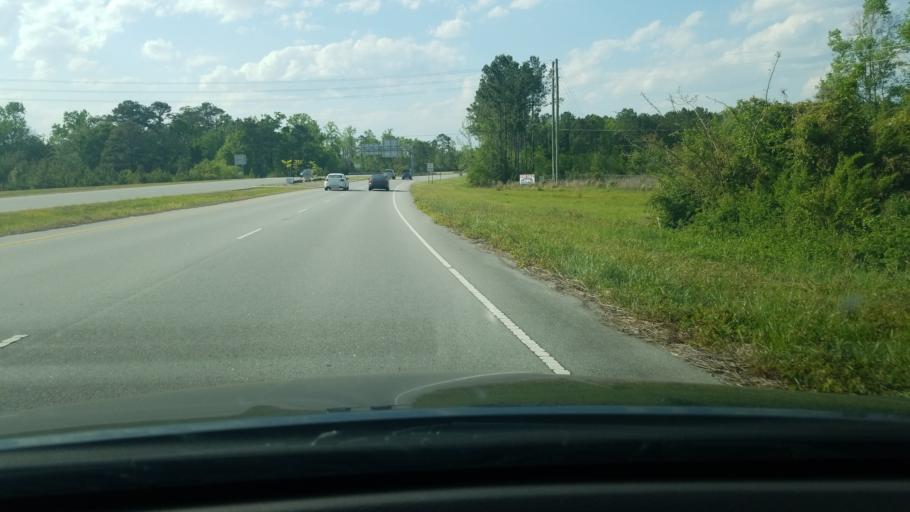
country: US
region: North Carolina
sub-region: Onslow County
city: Pumpkin Center
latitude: 34.7749
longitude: -77.3994
